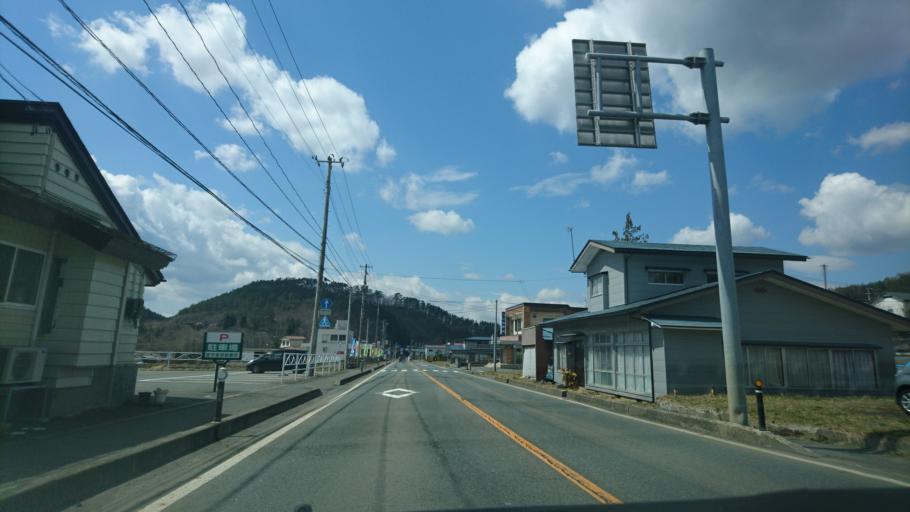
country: JP
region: Iwate
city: Tono
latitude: 39.3456
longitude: 141.3562
